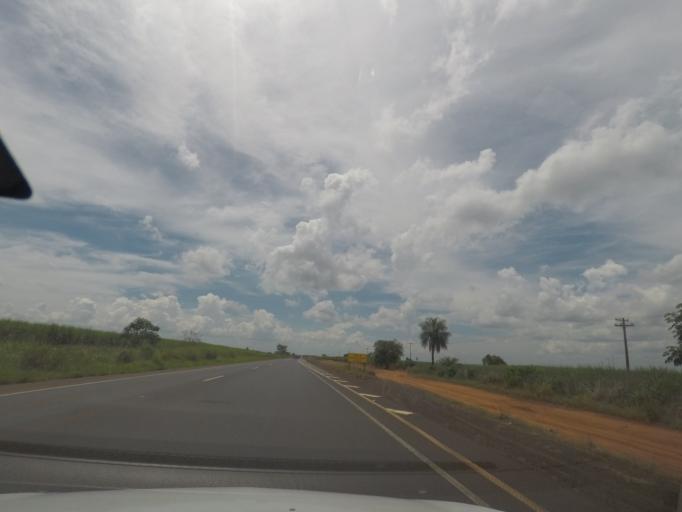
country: BR
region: Sao Paulo
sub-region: Barretos
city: Barretos
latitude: -20.3910
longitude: -48.6396
